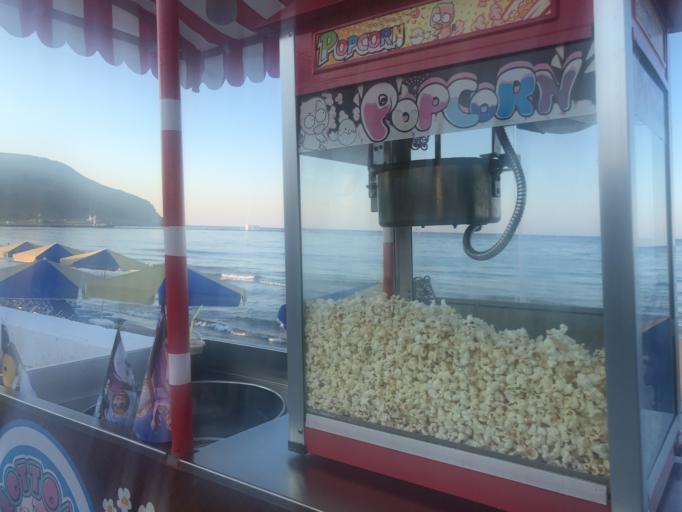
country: GR
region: Crete
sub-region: Nomos Chanias
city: Georgioupolis
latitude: 35.3621
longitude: 24.2630
